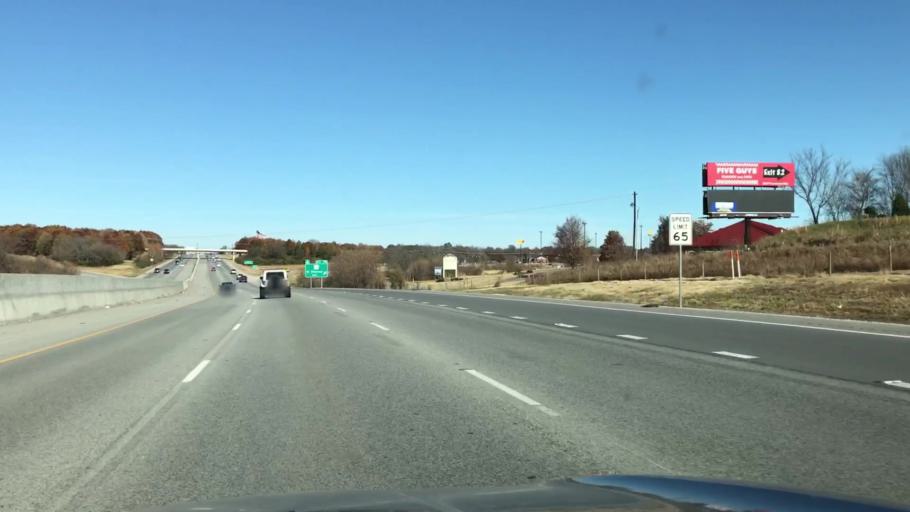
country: US
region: Arkansas
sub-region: Benton County
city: Lowell
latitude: 36.2481
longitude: -94.1505
